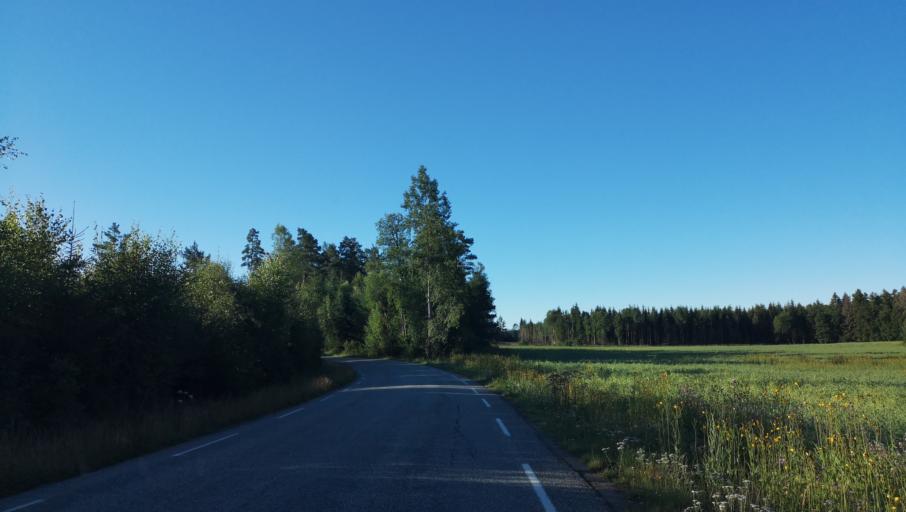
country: NO
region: Ostfold
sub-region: Hobol
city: Knappstad
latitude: 59.6397
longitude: 11.0166
